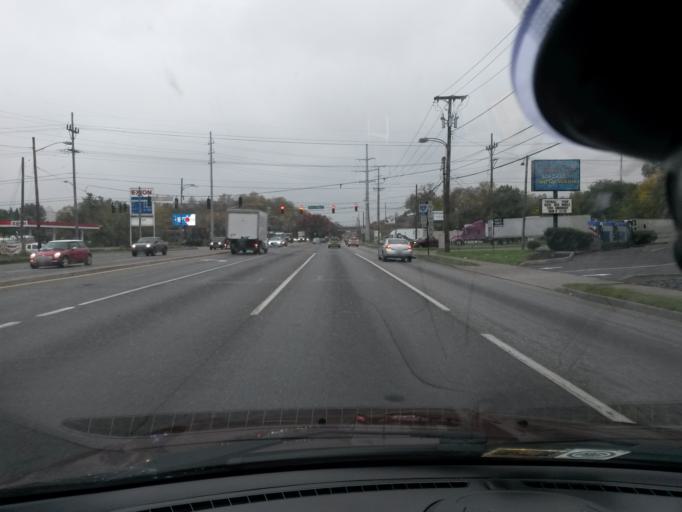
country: US
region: Virginia
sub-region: City of Roanoke
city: Roanoke
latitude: 37.2832
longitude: -79.9240
